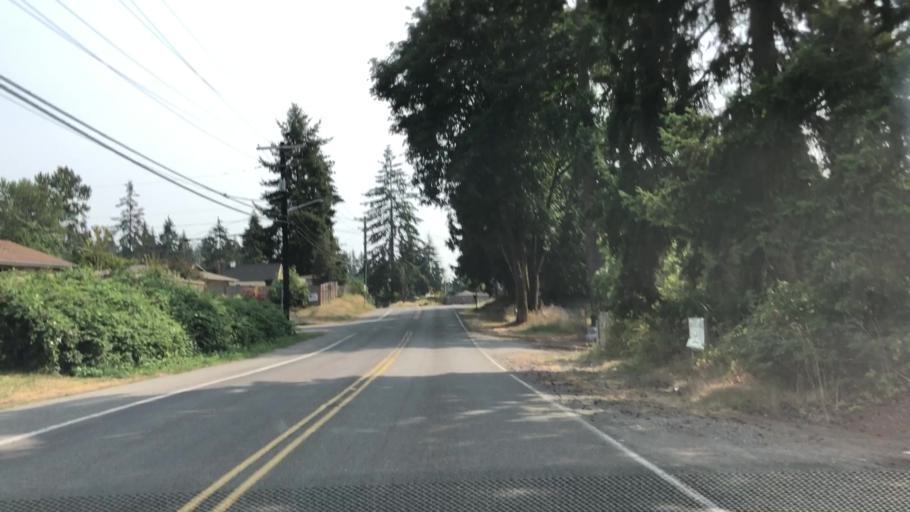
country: US
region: Washington
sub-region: Snohomish County
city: Brier
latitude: 47.8063
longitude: -122.2537
